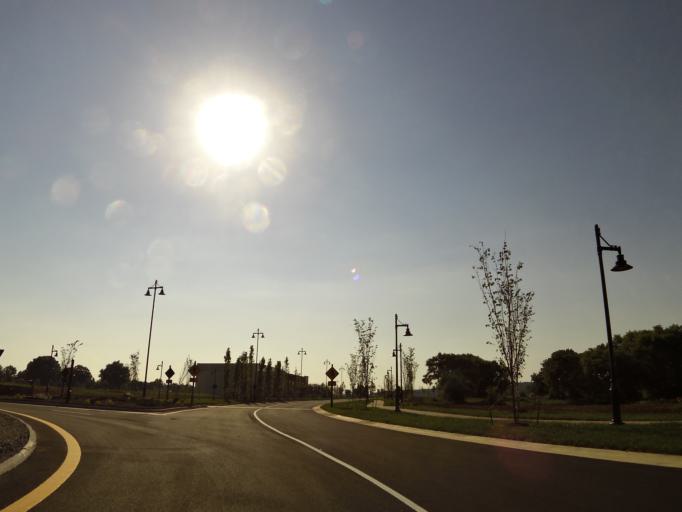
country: US
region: Tennessee
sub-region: Blount County
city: Eagleton Village
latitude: 35.7994
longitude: -83.9310
